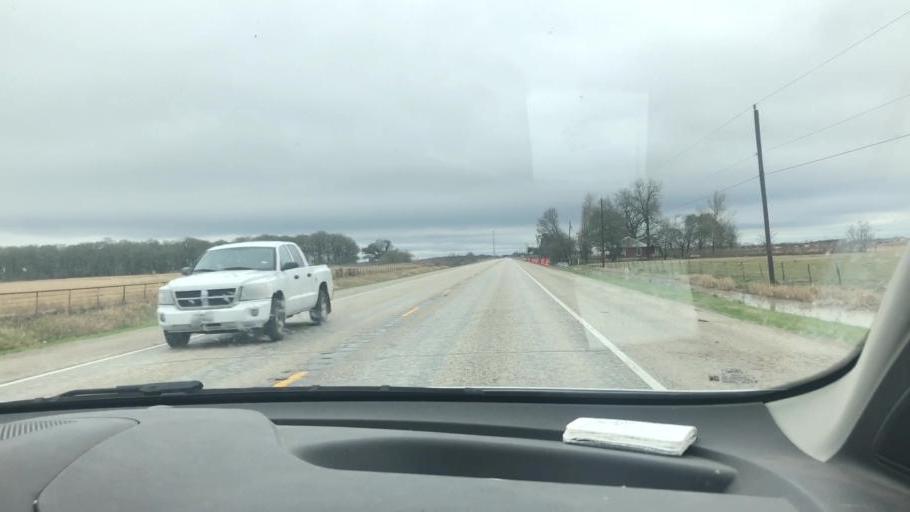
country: US
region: Texas
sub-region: Wharton County
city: Wharton
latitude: 29.2474
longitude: -96.0462
